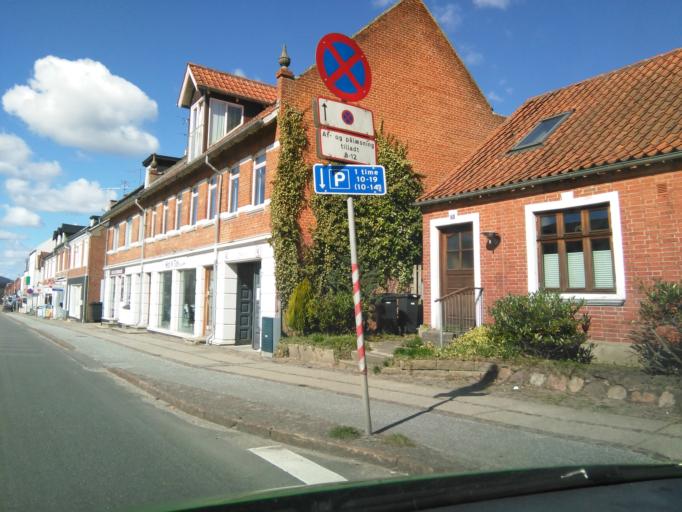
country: DK
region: Central Jutland
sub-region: Skanderborg Kommune
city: Ry
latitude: 56.0918
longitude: 9.7604
